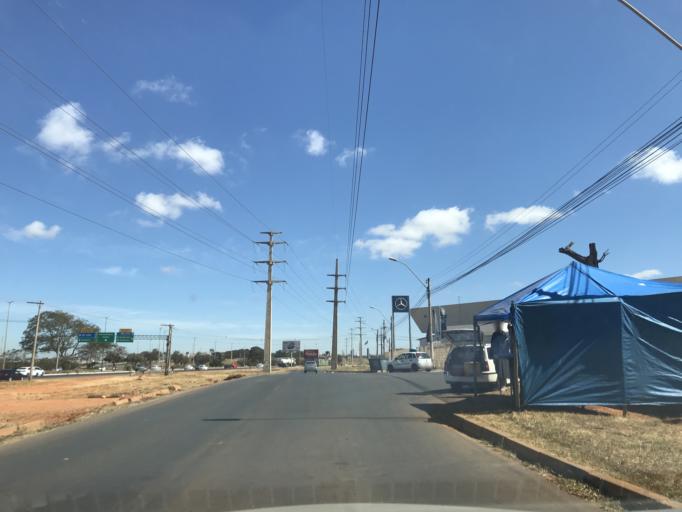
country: BR
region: Federal District
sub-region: Brasilia
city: Brasilia
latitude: -15.8762
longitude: -48.0227
